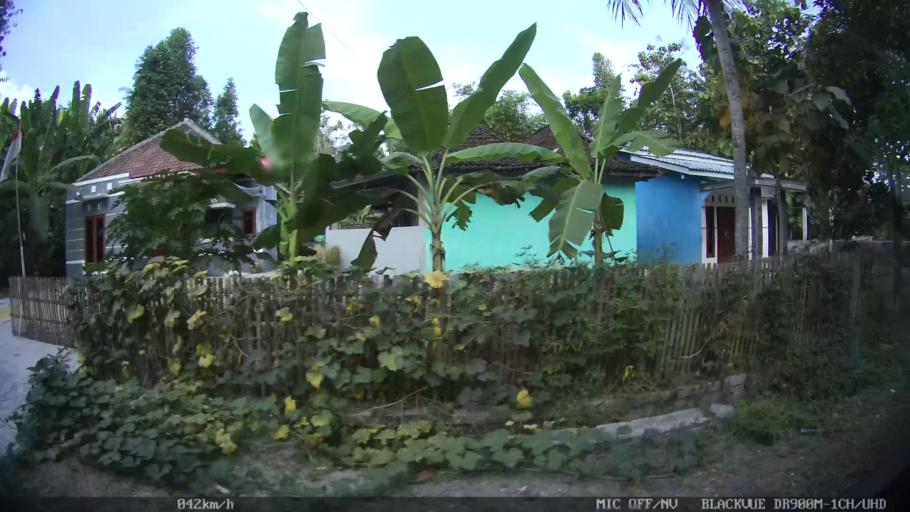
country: ID
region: Daerah Istimewa Yogyakarta
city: Bantul
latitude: -7.8616
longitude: 110.3193
